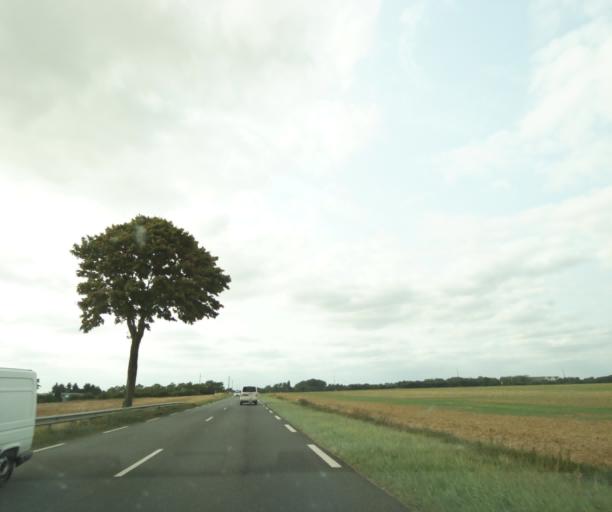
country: FR
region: Centre
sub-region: Departement d'Indre-et-Loire
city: Reignac-sur-Indre
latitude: 47.2047
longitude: 0.9081
